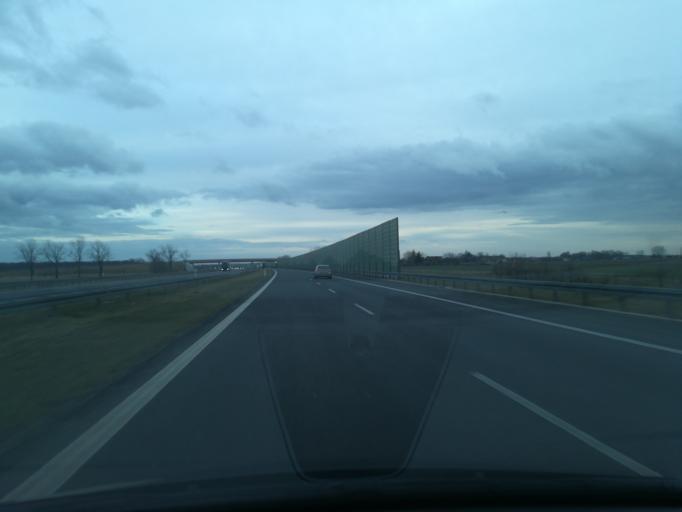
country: PL
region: Lodz Voivodeship
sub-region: Powiat kutnowski
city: Krzyzanow
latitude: 52.1515
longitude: 19.4815
